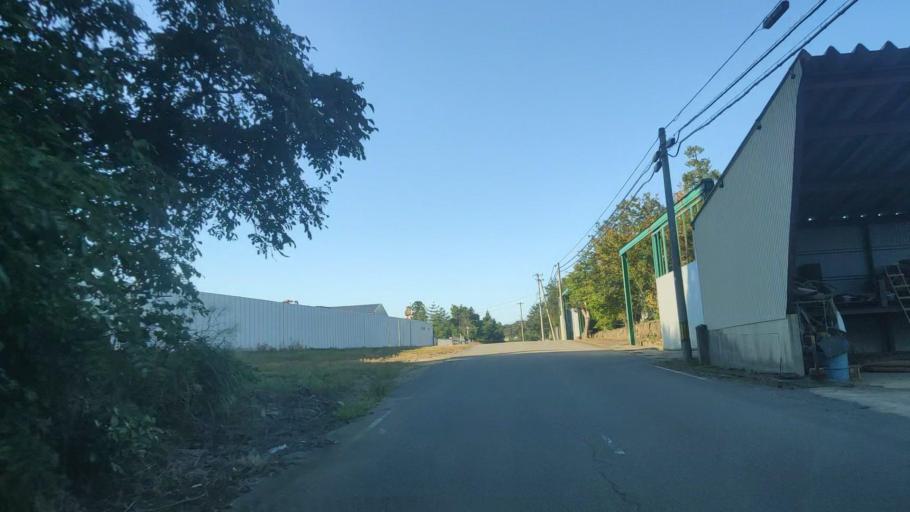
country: JP
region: Ishikawa
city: Nanao
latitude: 37.1276
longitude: 136.9314
